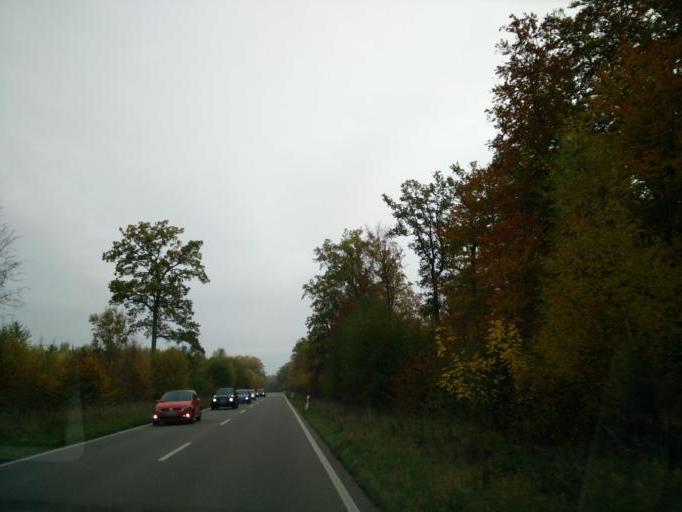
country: DE
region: Baden-Wuerttemberg
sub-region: Tuebingen Region
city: Dettenhausen
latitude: 48.5659
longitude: 9.1033
